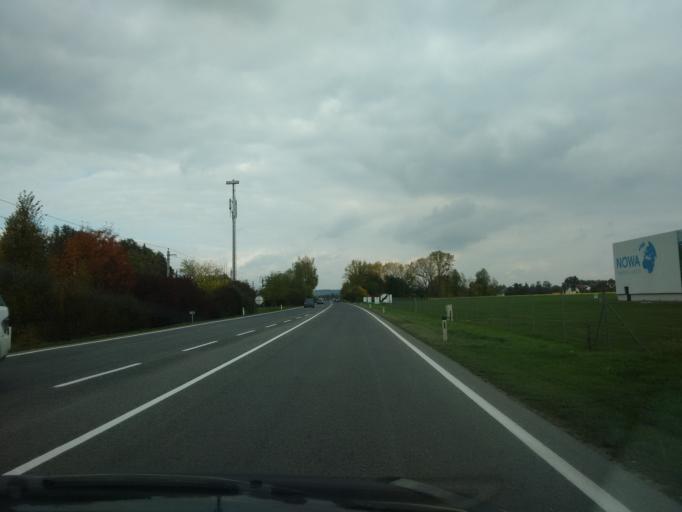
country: AT
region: Upper Austria
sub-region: Politischer Bezirk Vocklabruck
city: Redlham
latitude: 48.0340
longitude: 13.7415
